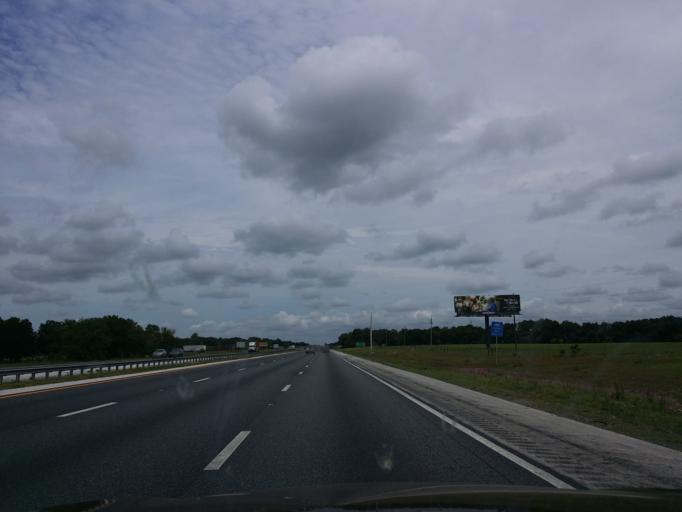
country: US
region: Florida
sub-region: Sumter County
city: Wildwood
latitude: 28.8855
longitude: -82.0950
